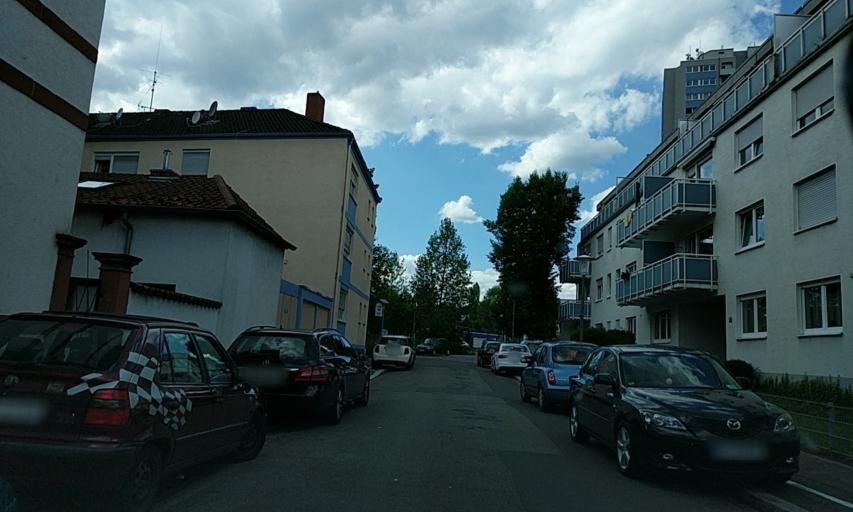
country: DE
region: Rheinland-Pfalz
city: Kaiserslautern
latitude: 49.4485
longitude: 7.7799
